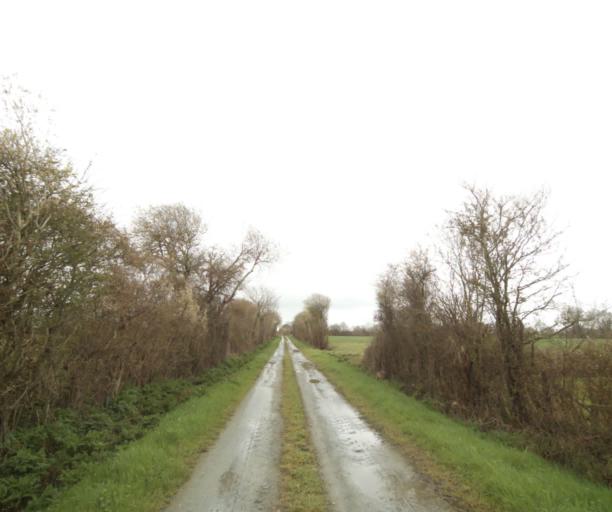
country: FR
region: Pays de la Loire
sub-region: Departement de la Loire-Atlantique
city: Bouvron
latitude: 47.4463
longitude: -1.8559
